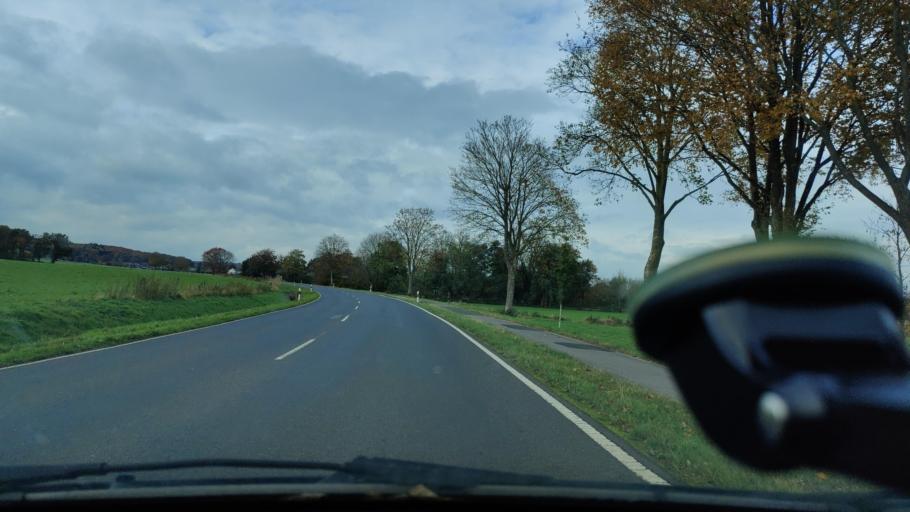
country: DE
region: North Rhine-Westphalia
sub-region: Regierungsbezirk Dusseldorf
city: Sonsbeck
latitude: 51.6400
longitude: 6.3913
